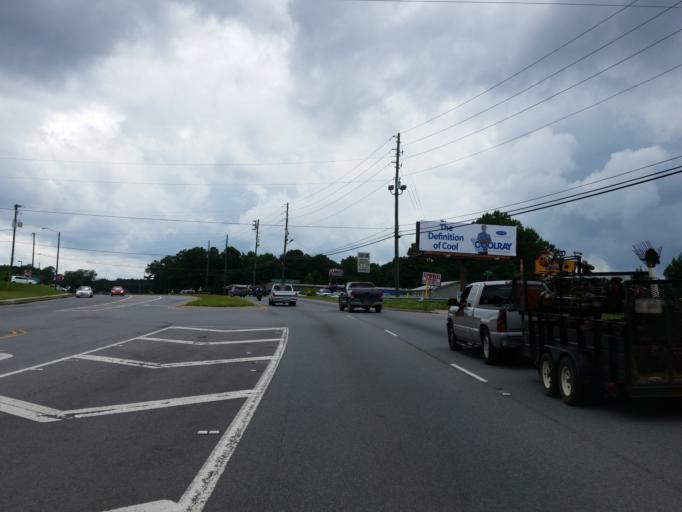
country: US
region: Georgia
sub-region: Cherokee County
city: Woodstock
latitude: 34.0853
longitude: -84.5566
